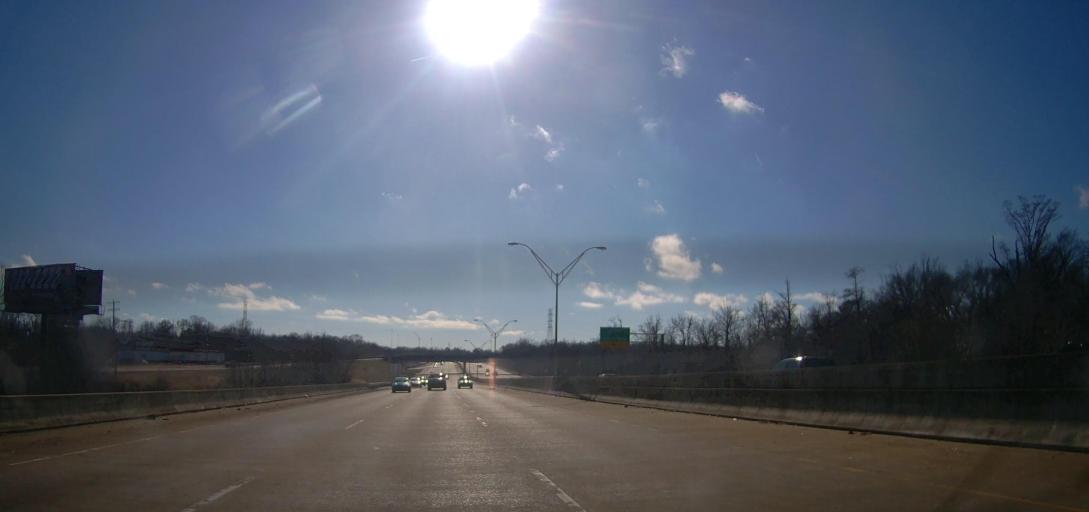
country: US
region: Tennessee
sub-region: Shelby County
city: Bartlett
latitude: 35.2010
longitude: -89.9243
